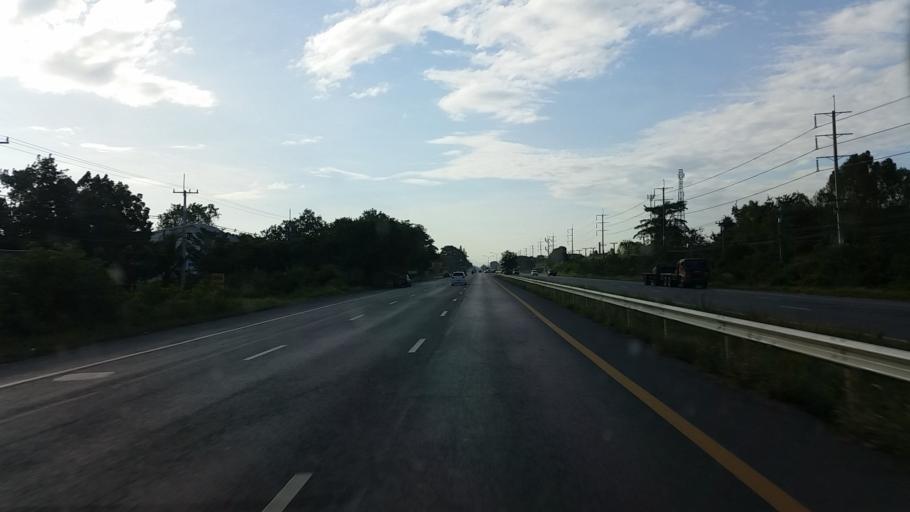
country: TH
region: Sara Buri
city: Chaloem Phra Kiat
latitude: 14.6257
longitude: 100.8902
